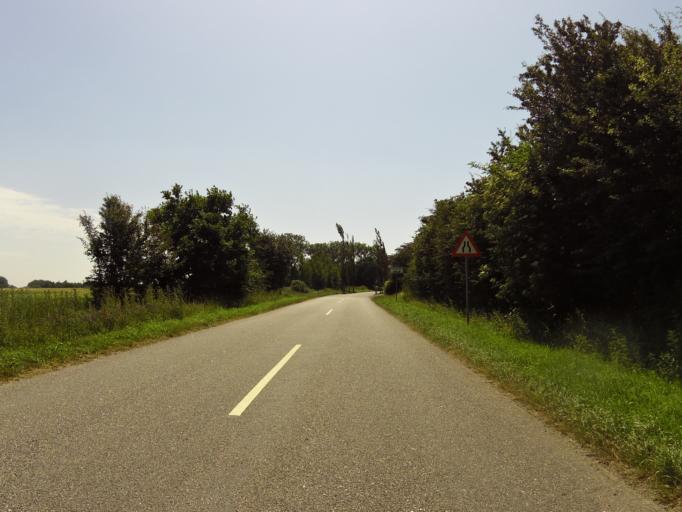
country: DK
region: South Denmark
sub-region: Haderslev Kommune
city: Vojens
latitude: 55.1617
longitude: 9.2151
